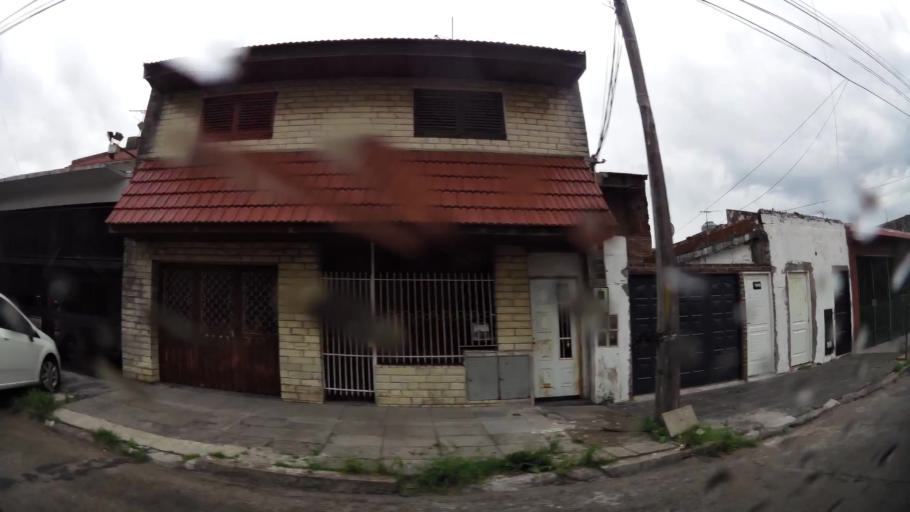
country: AR
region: Buenos Aires
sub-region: Partido de Lanus
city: Lanus
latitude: -34.6870
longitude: -58.4009
